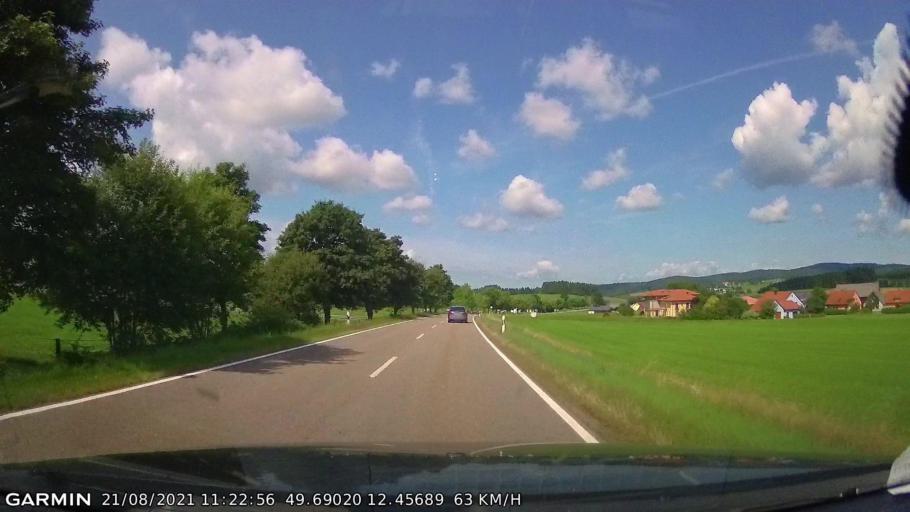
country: DE
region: Bavaria
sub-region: Upper Palatinate
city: Georgenberg
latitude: 49.6902
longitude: 12.4567
